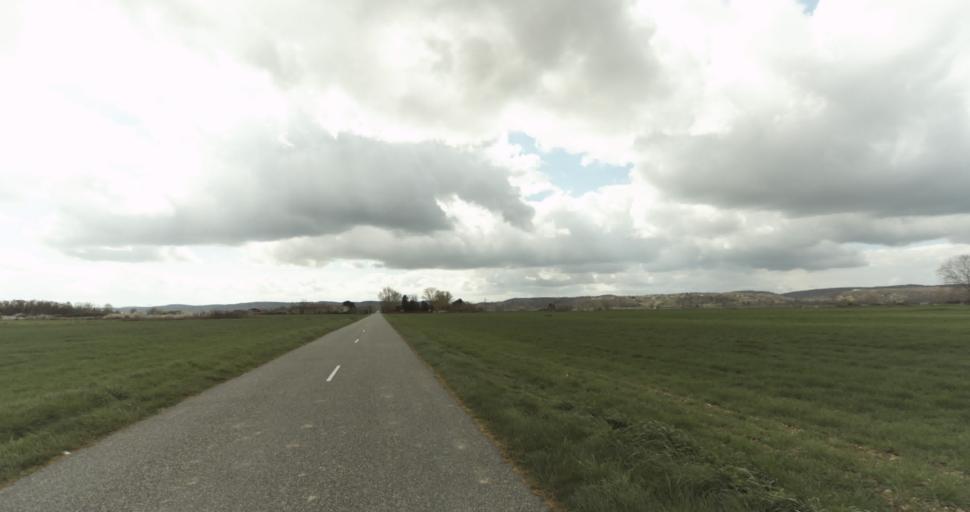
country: FR
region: Midi-Pyrenees
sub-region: Departement de la Haute-Garonne
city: Auterive
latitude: 43.3252
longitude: 1.4767
